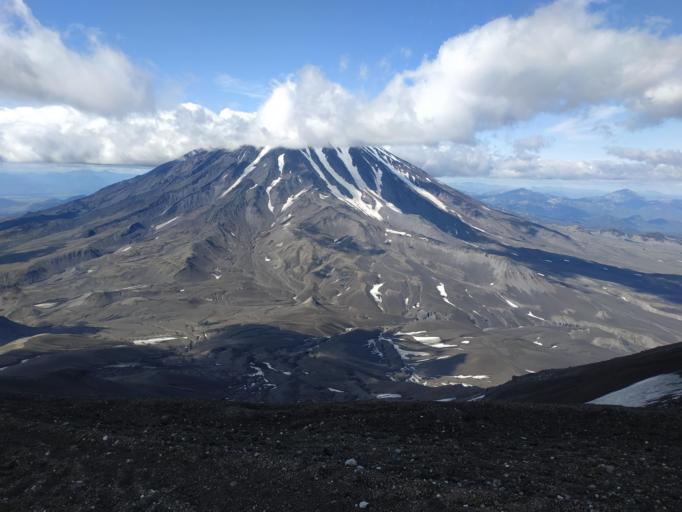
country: RU
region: Kamtsjatka
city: Petropavlovsk-Kamchatsky
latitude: 53.2663
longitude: 158.8115
